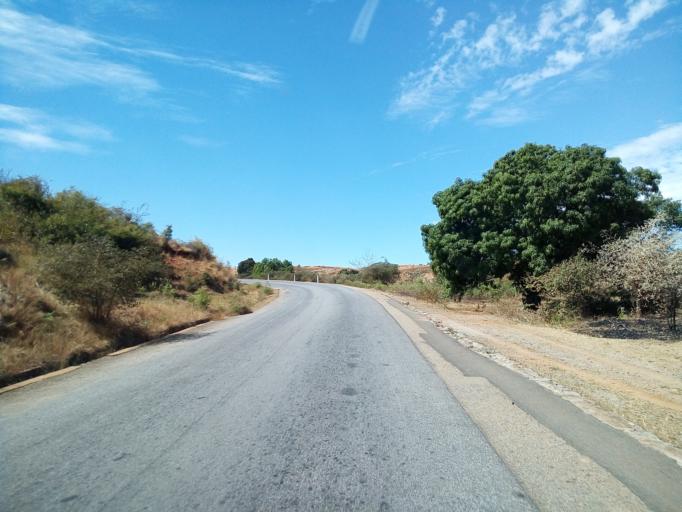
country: MG
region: Betsiboka
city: Maevatanana
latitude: -16.9220
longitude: 46.8647
